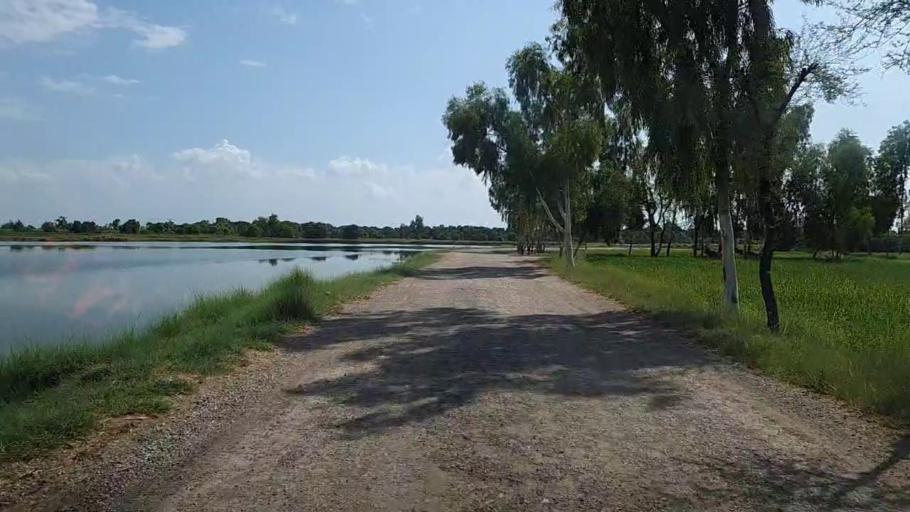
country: PK
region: Sindh
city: Bhiria
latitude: 26.9128
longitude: 68.2273
